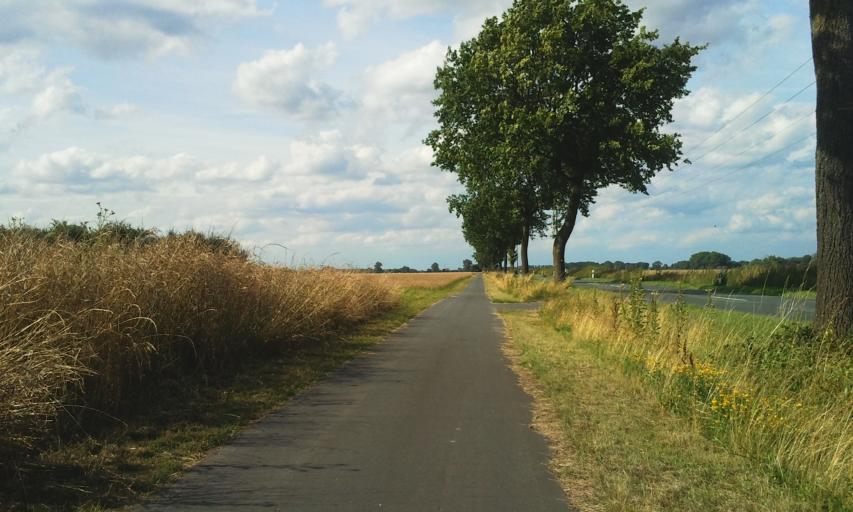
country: DE
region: Lower Saxony
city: Drakenburg
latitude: 52.6926
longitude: 9.2106
